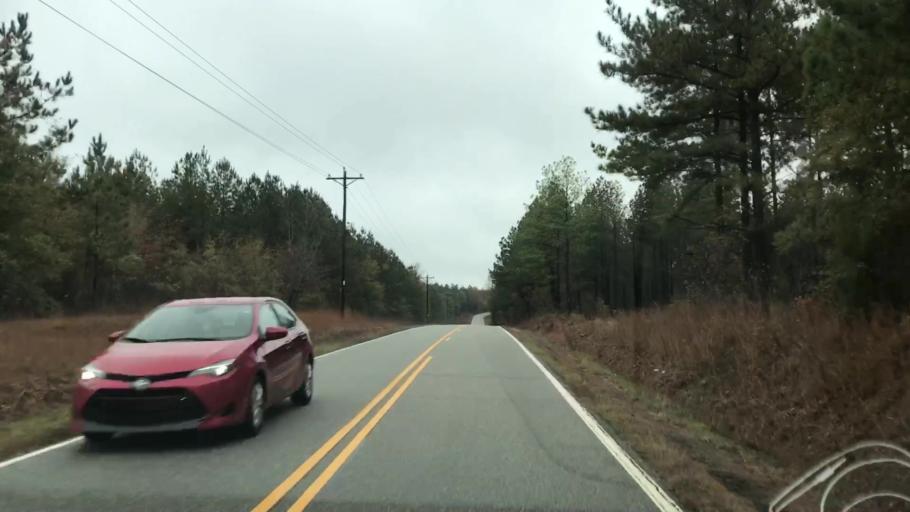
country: US
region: South Carolina
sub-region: Laurens County
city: Joanna
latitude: 34.3218
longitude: -81.8767
